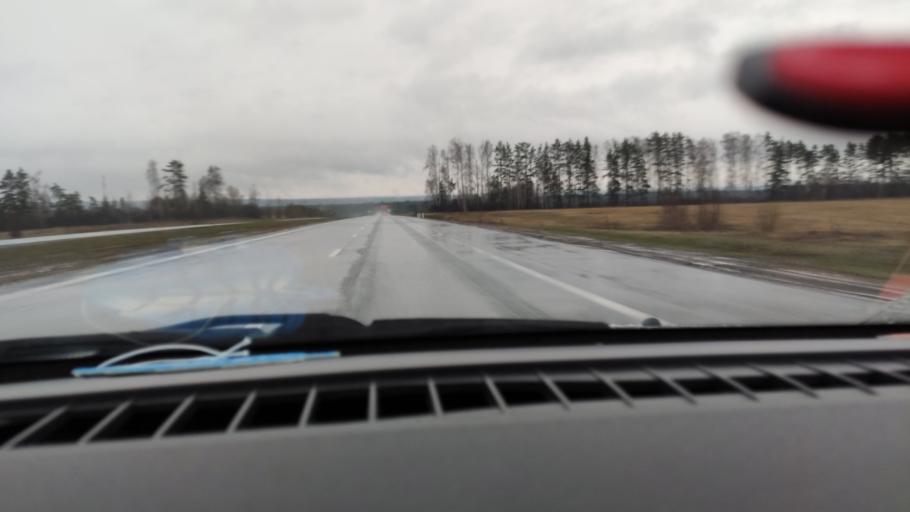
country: RU
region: Tatarstan
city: Yelabuga
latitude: 55.7841
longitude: 52.1714
